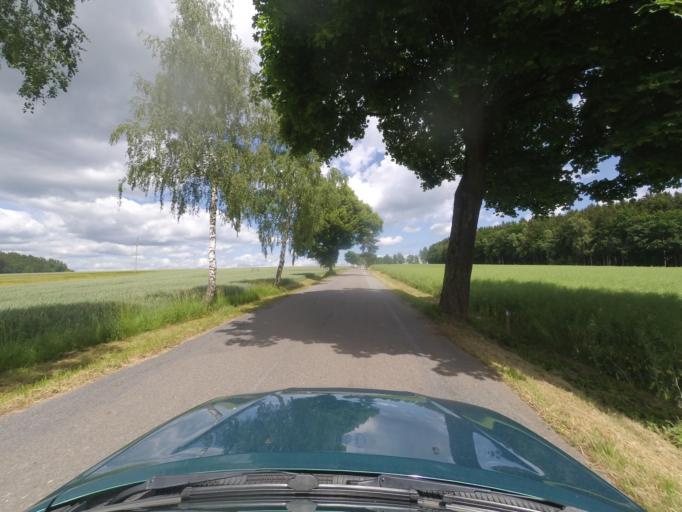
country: CZ
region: Pardubicky
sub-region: Okres Usti nad Orlici
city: Kunvald
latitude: 50.1019
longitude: 16.5269
